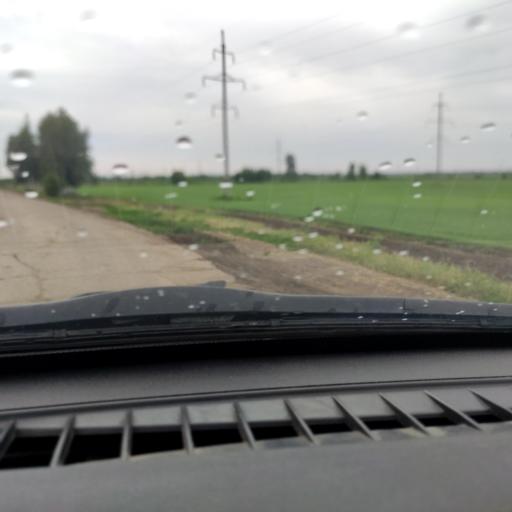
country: RU
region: Samara
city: Tol'yatti
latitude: 53.5938
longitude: 49.4365
